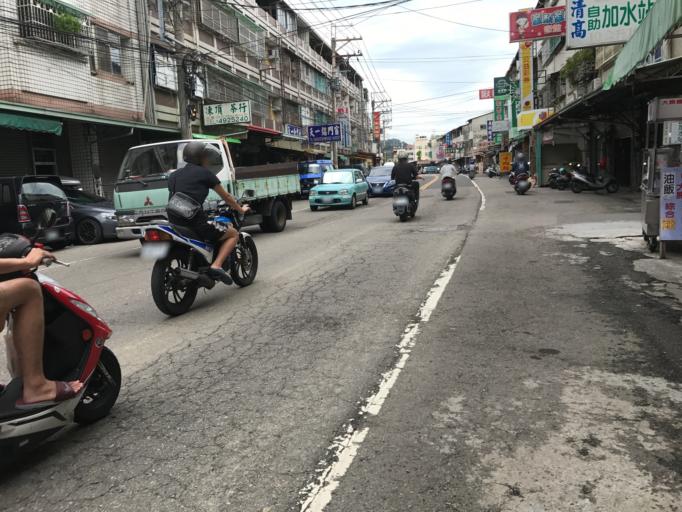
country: TW
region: Taiwan
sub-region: Taichung City
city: Taichung
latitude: 24.0864
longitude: 120.7086
